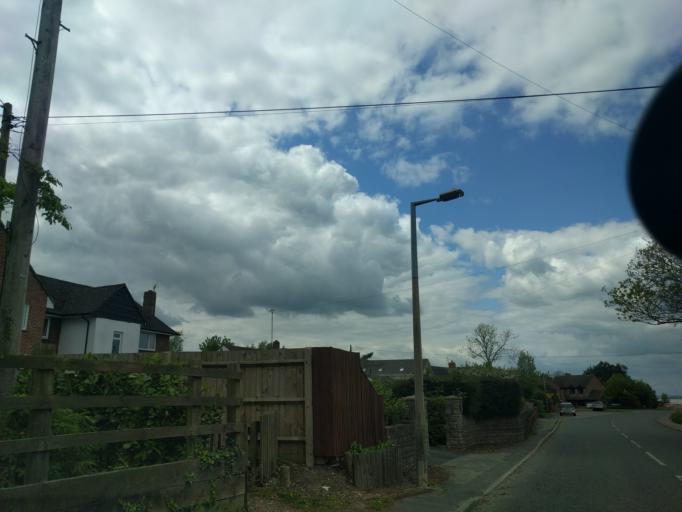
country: GB
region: England
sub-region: Wiltshire
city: Royal Wootton Bassett
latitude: 51.5388
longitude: -1.9108
